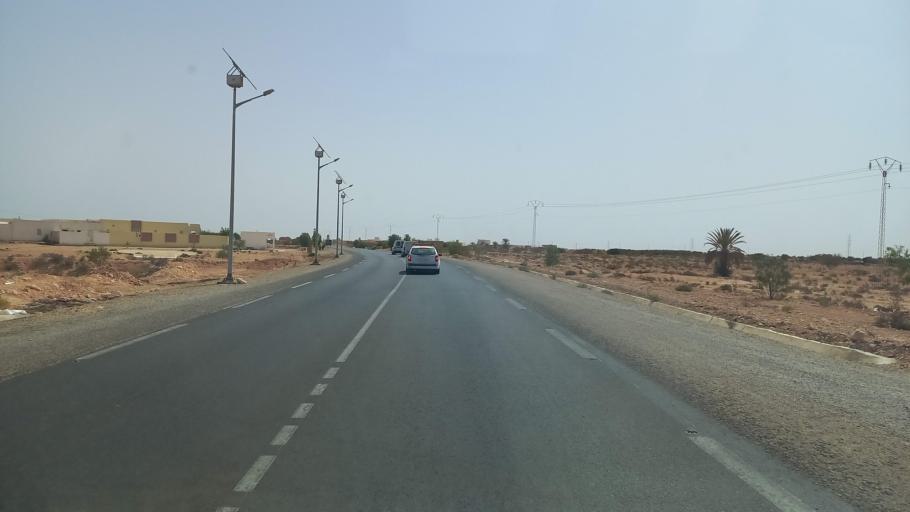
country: TN
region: Madanin
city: Medenine
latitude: 33.3696
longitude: 10.6810
